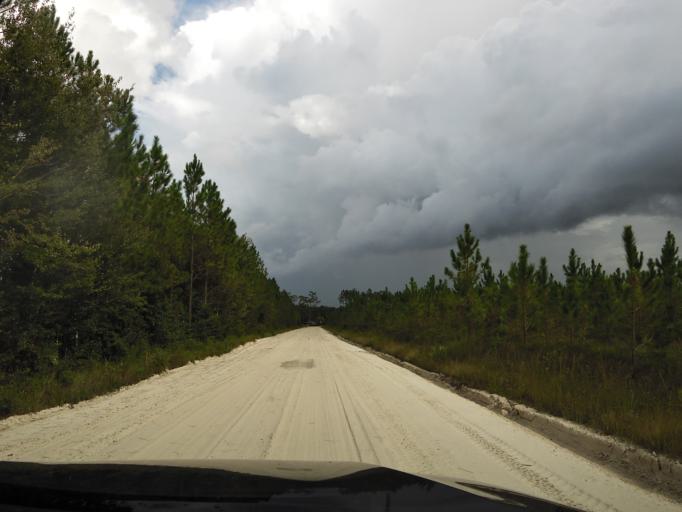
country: US
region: Florida
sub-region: Nassau County
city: Hilliard
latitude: 30.5938
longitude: -82.0516
